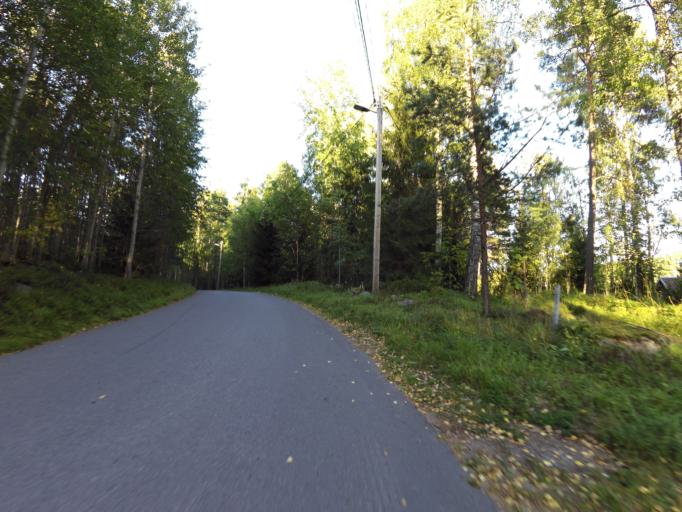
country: SE
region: Gaevleborg
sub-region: Gavle Kommun
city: Gavle
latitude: 60.7176
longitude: 17.1462
